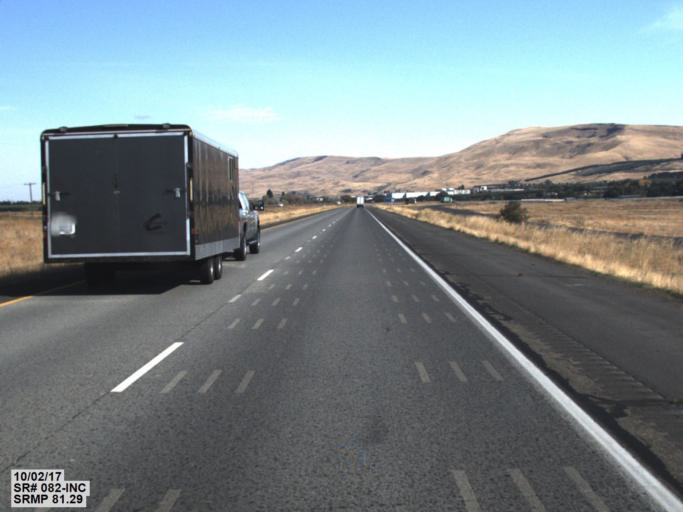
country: US
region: Washington
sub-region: Benton County
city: Prosser
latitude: 46.2211
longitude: -119.7625
